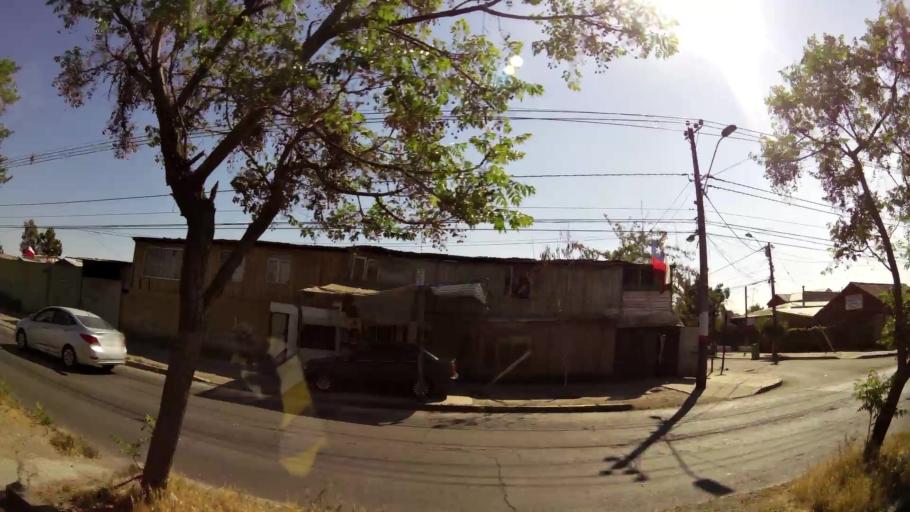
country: CL
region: Santiago Metropolitan
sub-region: Provincia de Santiago
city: La Pintana
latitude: -33.5320
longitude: -70.6100
